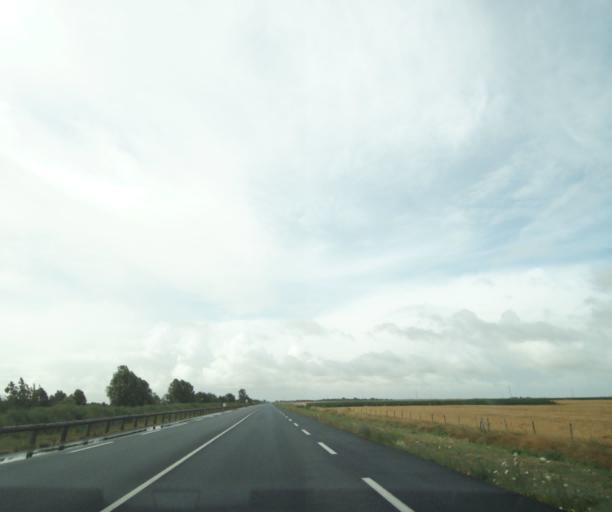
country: FR
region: Pays de la Loire
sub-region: Departement de la Vendee
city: Champagne-les-Marais
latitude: 46.3695
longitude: -1.0891
